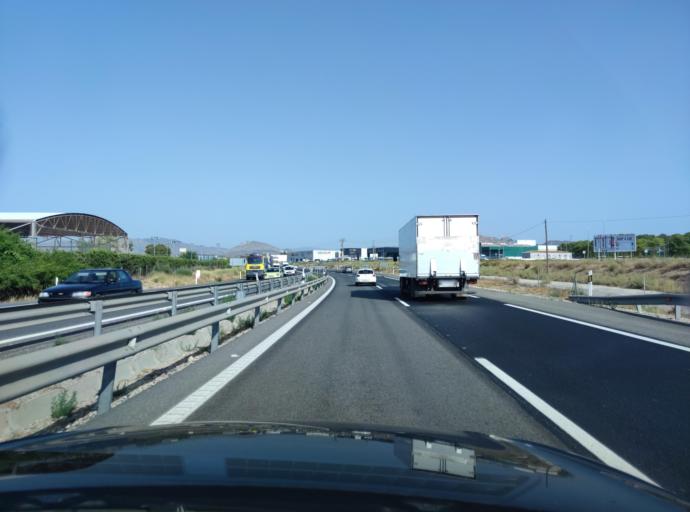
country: ES
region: Valencia
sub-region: Provincia de Alicante
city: Monforte del Cid
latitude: 38.3865
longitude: -0.7263
